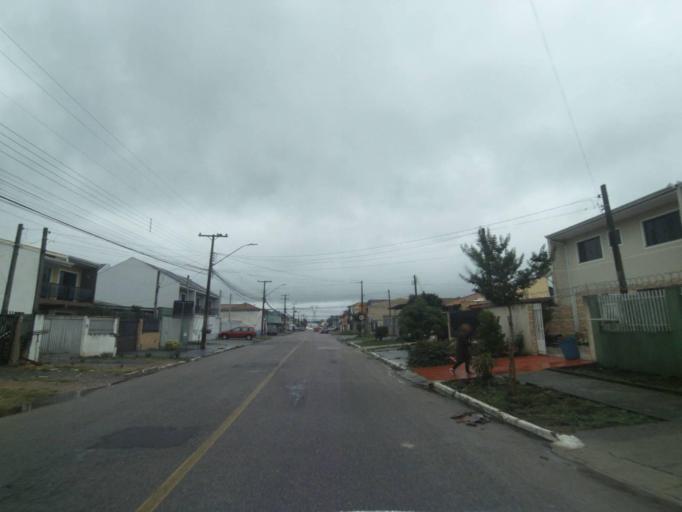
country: BR
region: Parana
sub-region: Araucaria
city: Araucaria
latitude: -25.5406
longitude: -49.3420
